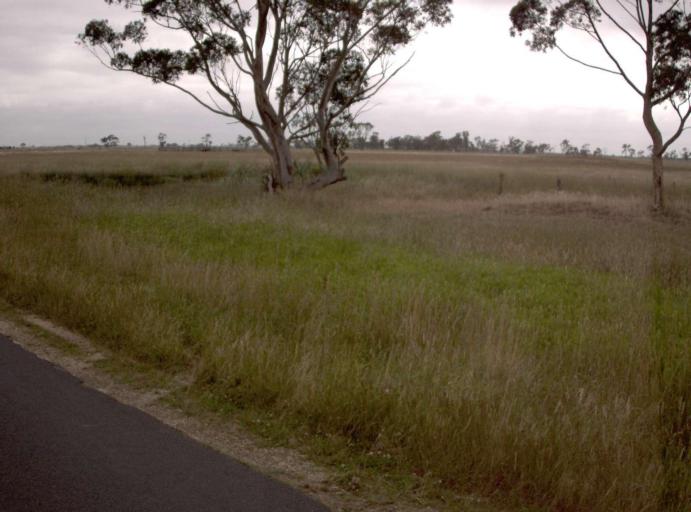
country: AU
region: Victoria
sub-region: Wellington
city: Heyfield
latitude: -38.1044
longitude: 146.7722
